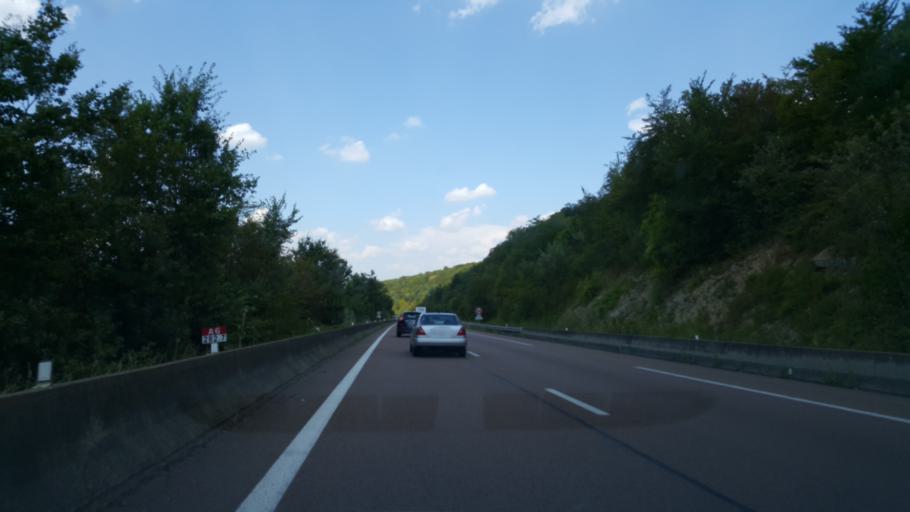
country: FR
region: Bourgogne
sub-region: Departement de la Cote-d'Or
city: Savigny-les-Beaune
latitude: 47.1363
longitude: 4.7000
